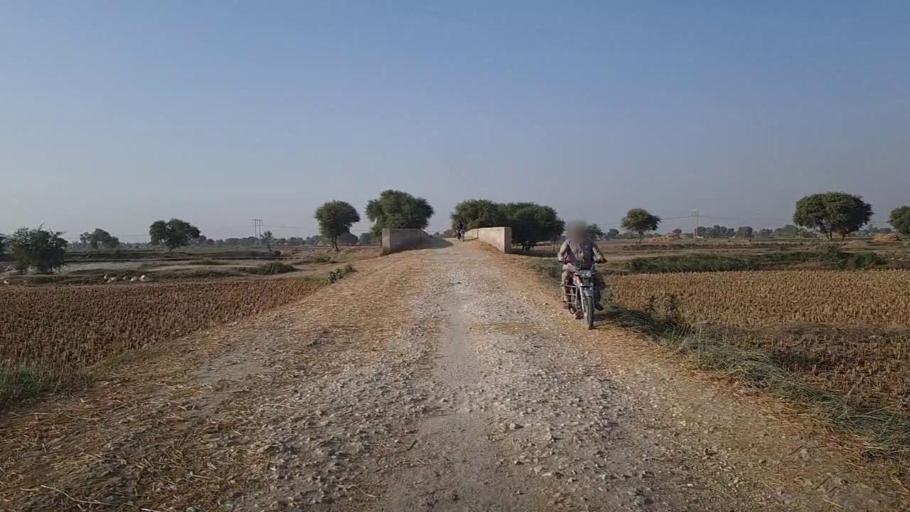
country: PK
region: Sindh
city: Kashmor
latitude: 28.4079
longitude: 69.4129
